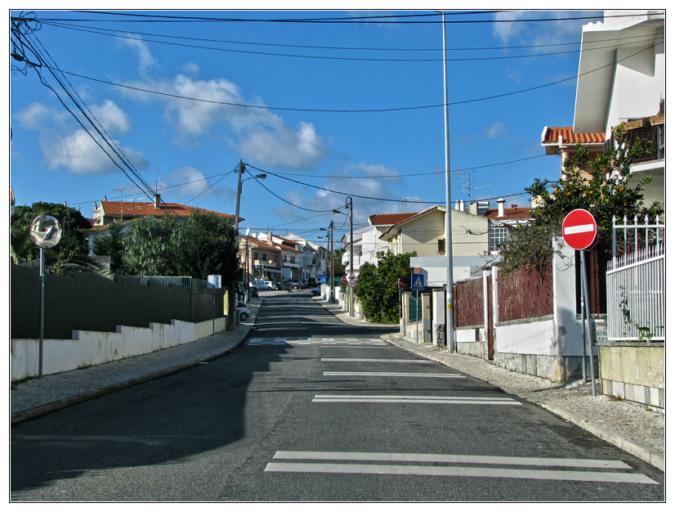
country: PT
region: Lisbon
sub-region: Cascais
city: Sao Domingos de Rana
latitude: 38.7013
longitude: -9.3390
